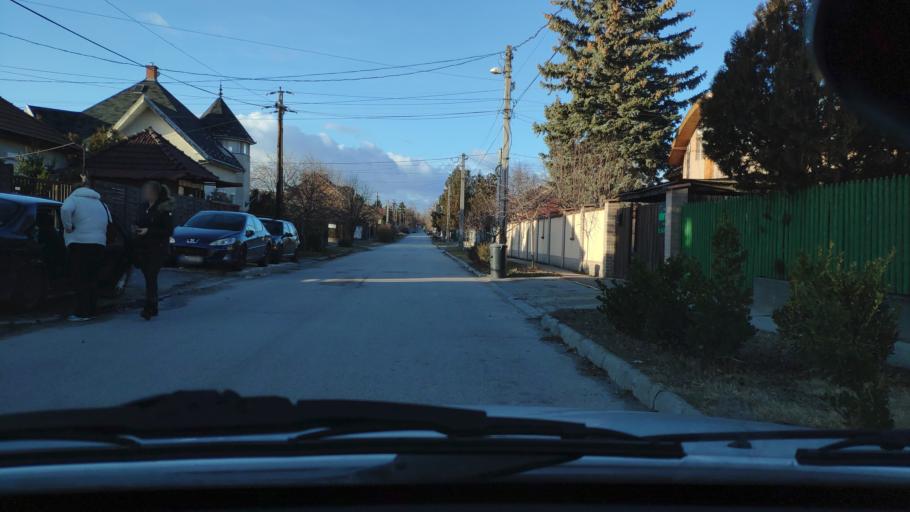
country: HU
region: Budapest
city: Budapest XXIII. keruelet
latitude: 47.3917
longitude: 19.1000
